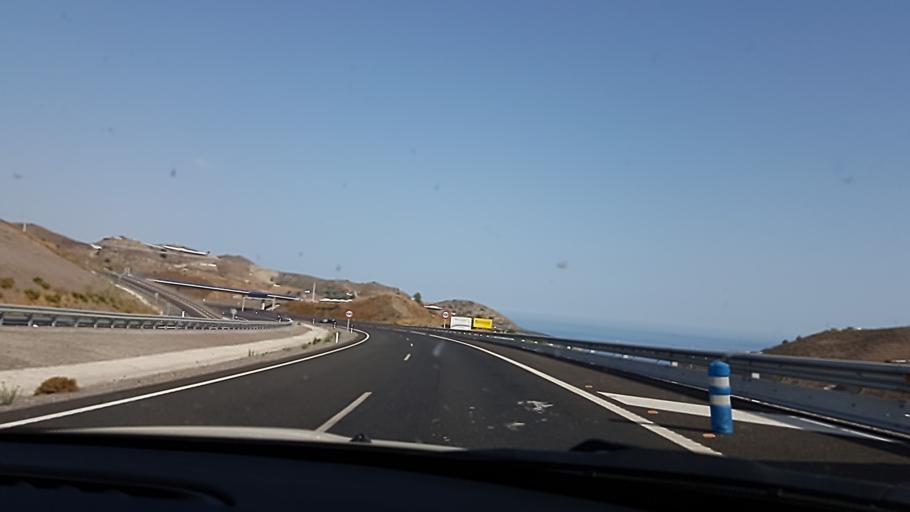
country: ES
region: Andalusia
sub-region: Provincia de Granada
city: Polopos
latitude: 36.7493
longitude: -3.3164
